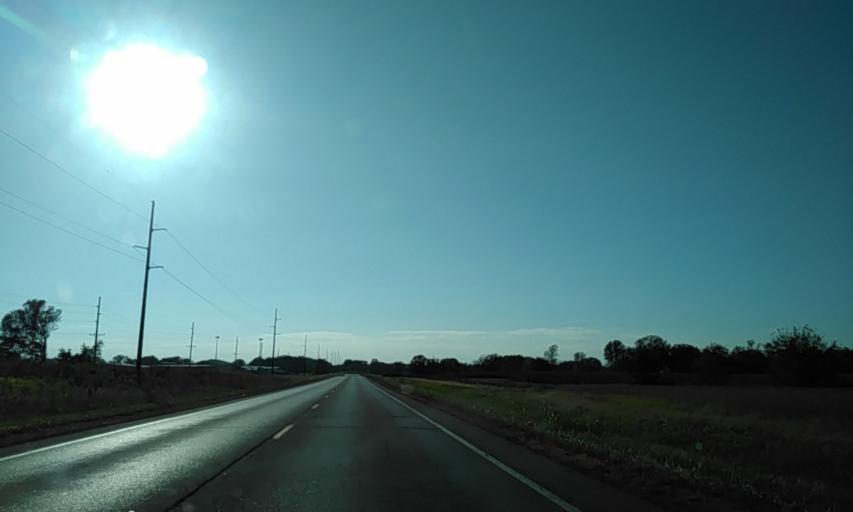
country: US
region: Illinois
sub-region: Madison County
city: Saint Jacob
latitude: 38.7171
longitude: -89.7908
